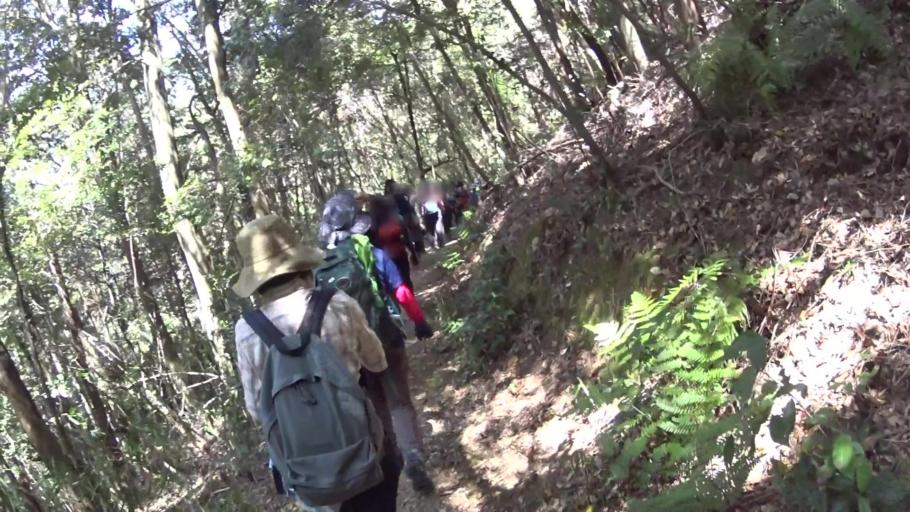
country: JP
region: Kyoto
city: Kyoto
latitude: 34.9853
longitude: 135.7862
